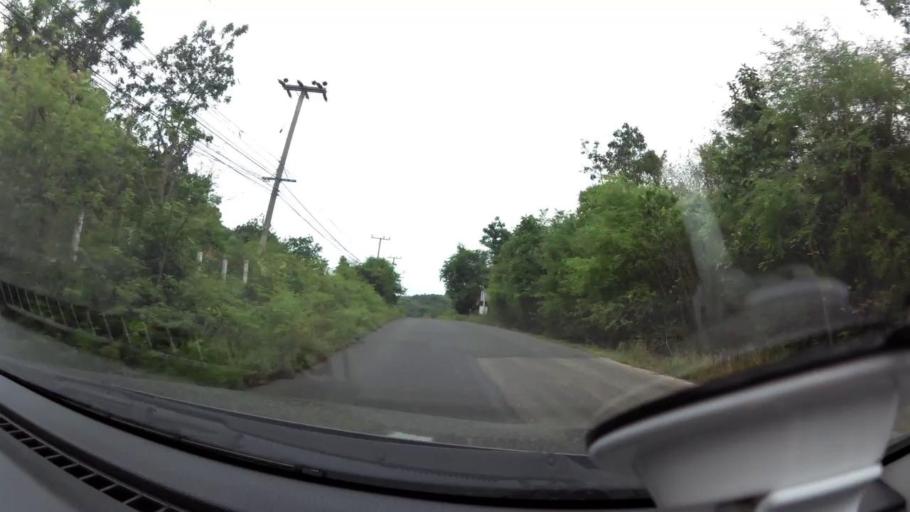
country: TH
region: Prachuap Khiri Khan
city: Pran Buri
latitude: 12.4391
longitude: 99.9710
